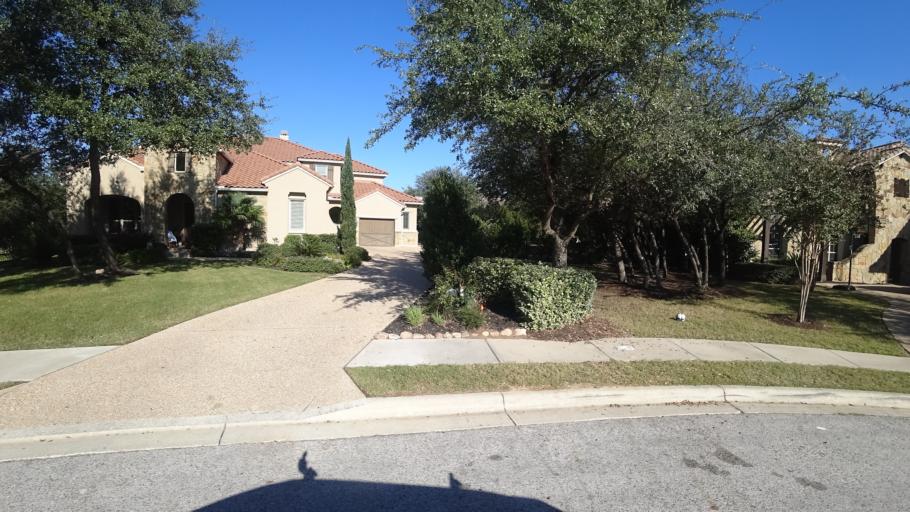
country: US
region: Texas
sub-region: Travis County
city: Barton Creek
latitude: 30.3509
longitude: -97.8885
